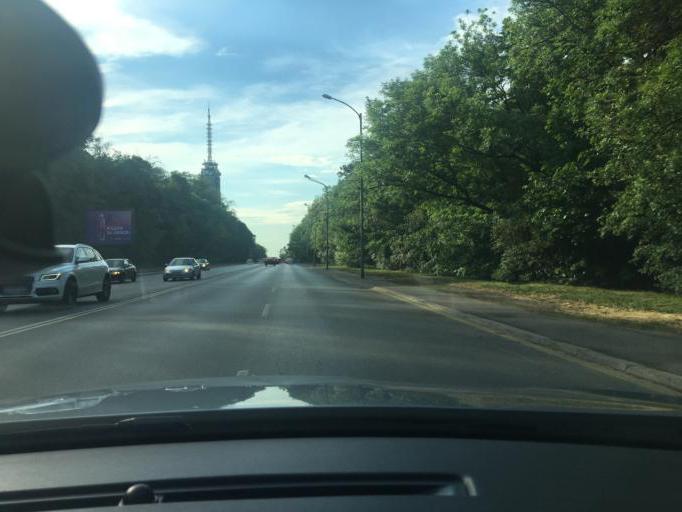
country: BG
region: Sofia-Capital
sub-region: Stolichna Obshtina
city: Sofia
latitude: 42.6742
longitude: 23.3460
